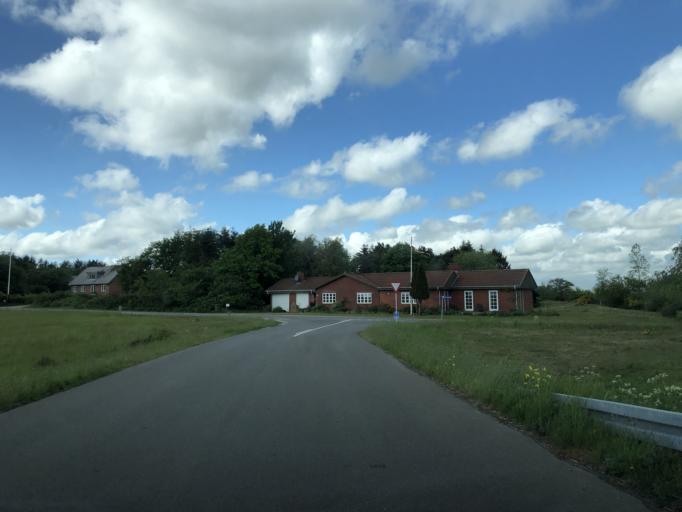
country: DK
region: Central Jutland
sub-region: Ringkobing-Skjern Kommune
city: Tarm
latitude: 55.9425
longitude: 8.5753
